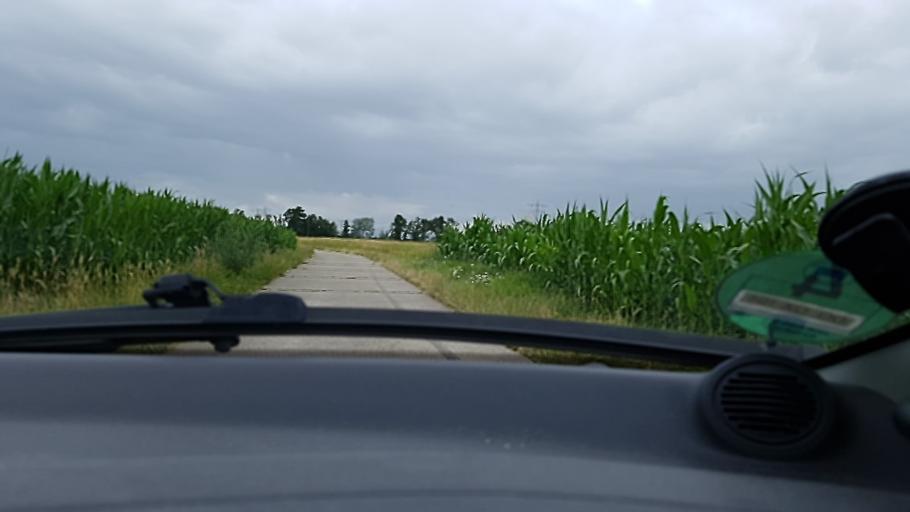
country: DE
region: Baden-Wuerttemberg
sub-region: Freiburg Region
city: Kehl
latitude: 48.5772
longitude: 7.8541
